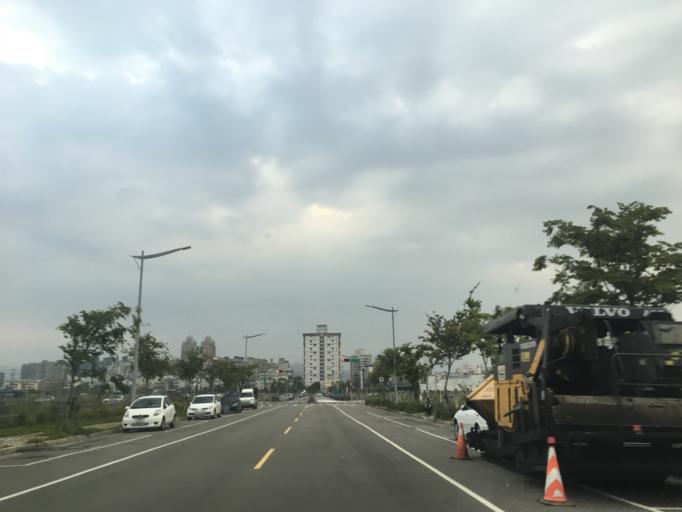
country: TW
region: Taiwan
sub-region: Taichung City
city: Taichung
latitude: 24.1868
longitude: 120.6923
